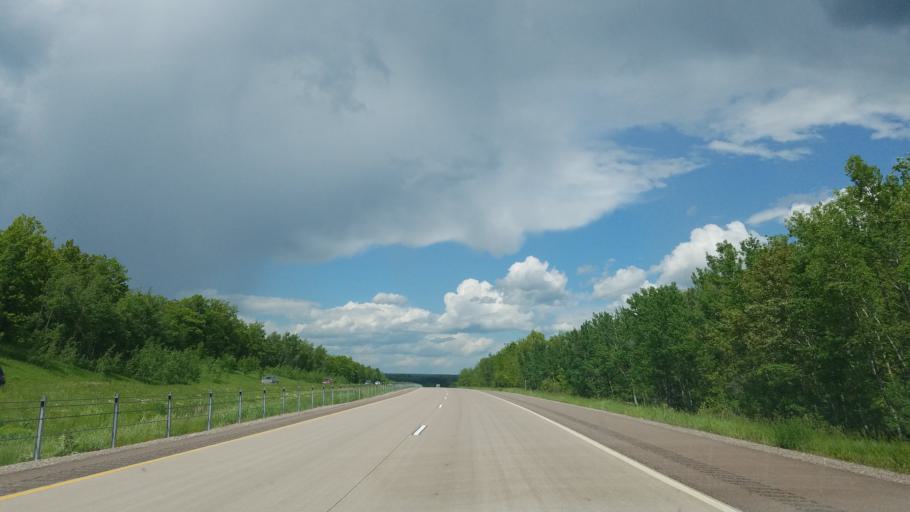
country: US
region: Minnesota
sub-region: Carlton County
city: Moose Lake
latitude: 46.4668
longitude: -92.7189
